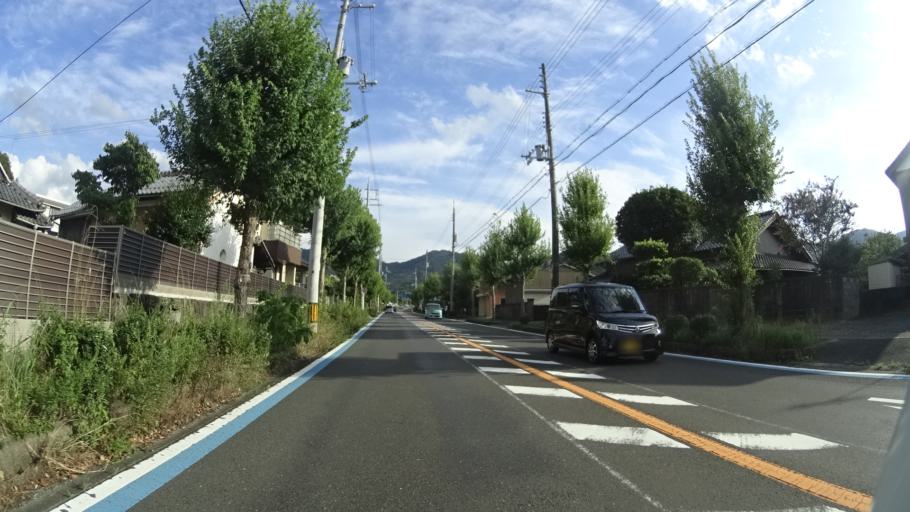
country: JP
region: Kyoto
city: Maizuru
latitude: 35.4562
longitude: 135.3969
